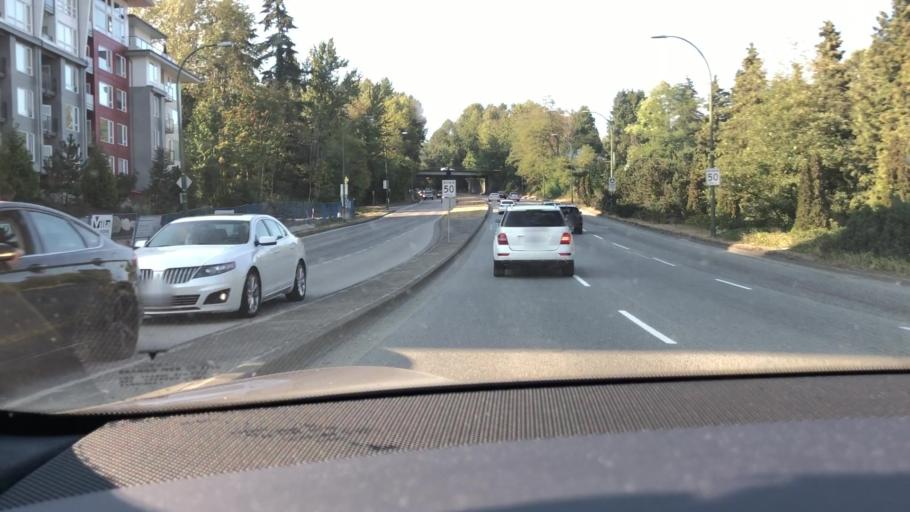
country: CA
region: British Columbia
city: Burnaby
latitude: 49.2058
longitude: -123.0234
